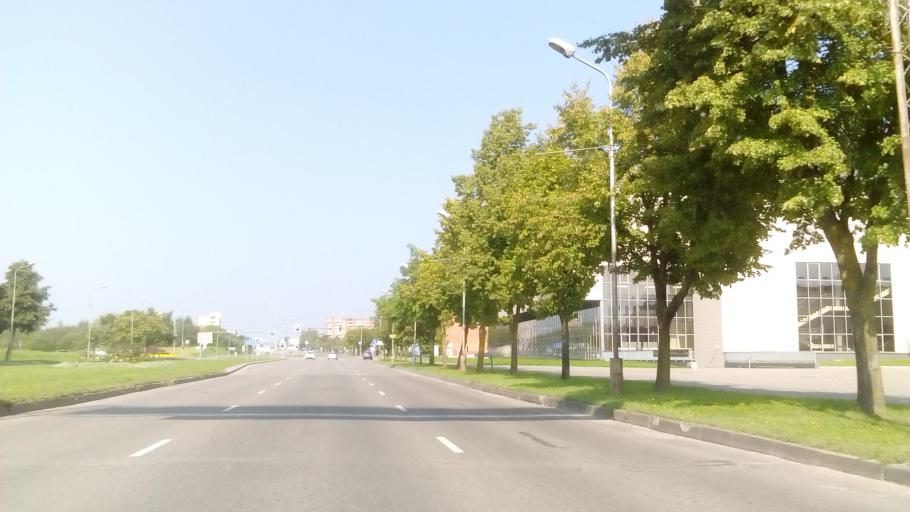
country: LT
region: Alytaus apskritis
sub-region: Alytus
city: Alytus
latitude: 54.4031
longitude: 24.0218
